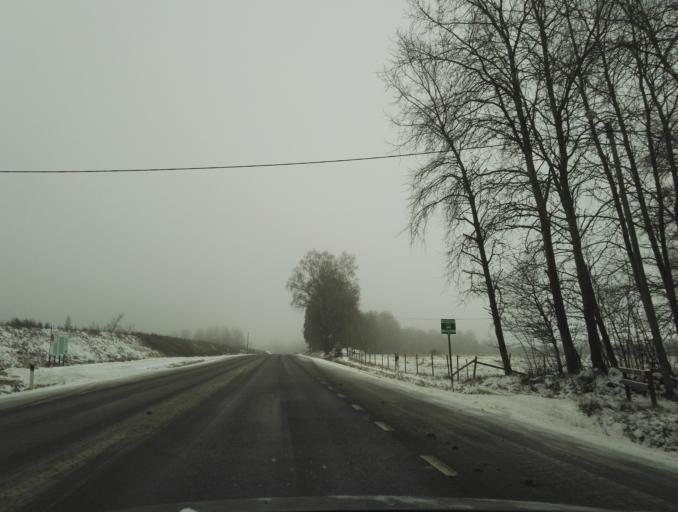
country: SE
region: Kronoberg
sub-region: Vaxjo Kommun
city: Vaexjoe
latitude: 56.8737
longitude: 14.7417
